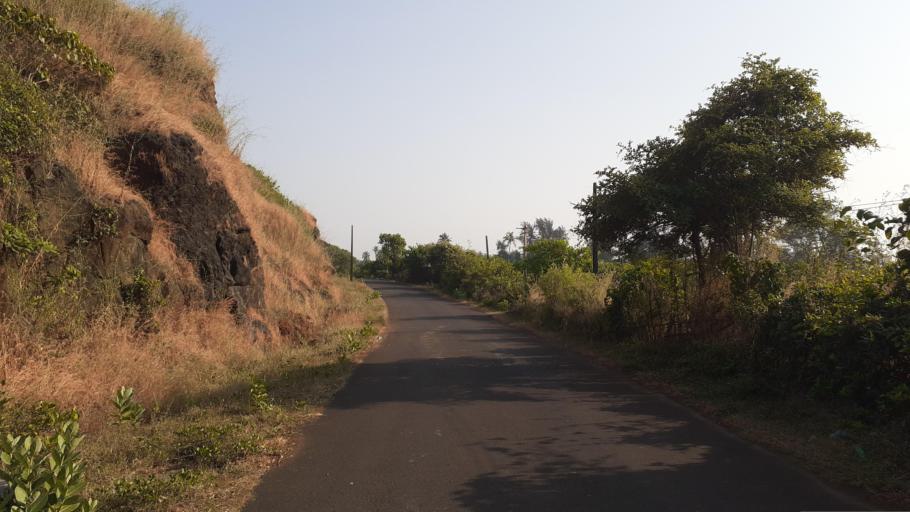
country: IN
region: Maharashtra
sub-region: Ratnagiri
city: Ratnagiri
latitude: 17.2215
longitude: 73.2450
